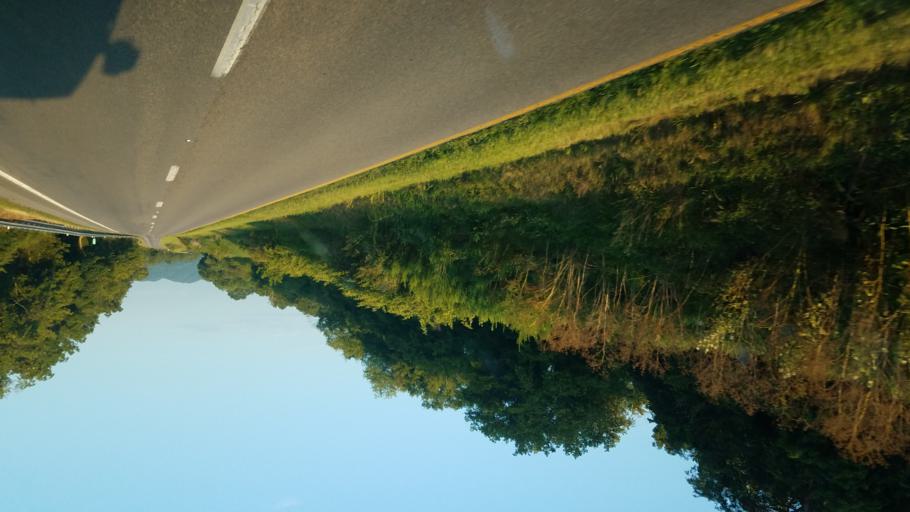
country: US
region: Virginia
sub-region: Scott County
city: Gate City
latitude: 36.6360
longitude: -82.6481
